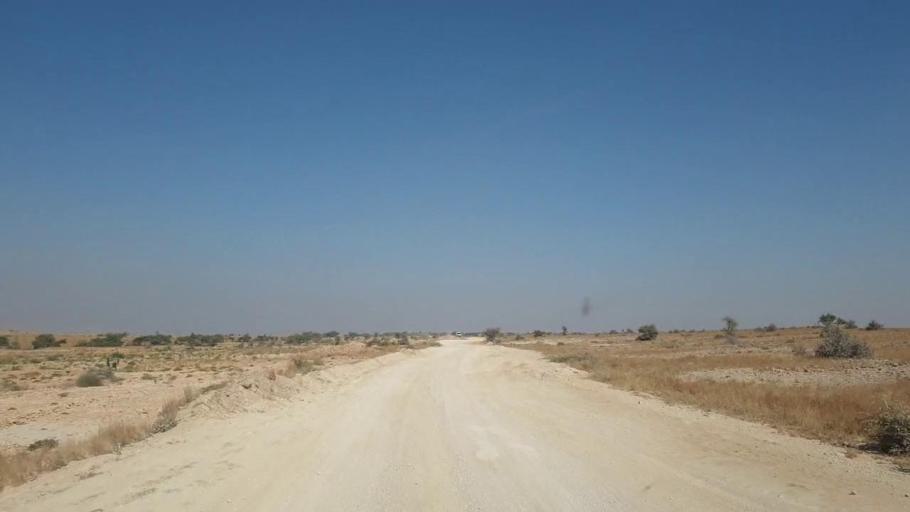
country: PK
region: Sindh
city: Thatta
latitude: 25.2285
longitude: 67.8033
